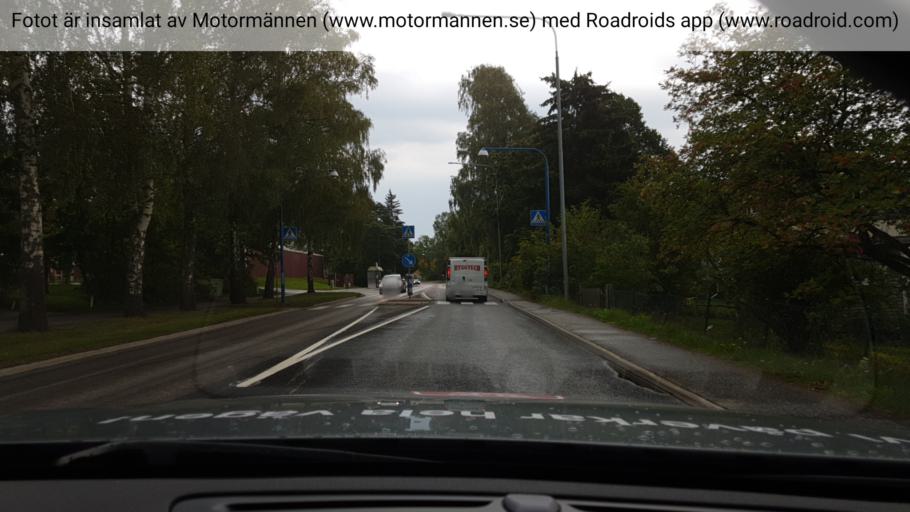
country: SE
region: Uppsala
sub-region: Habo Kommun
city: Balsta
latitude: 59.5732
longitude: 17.5201
